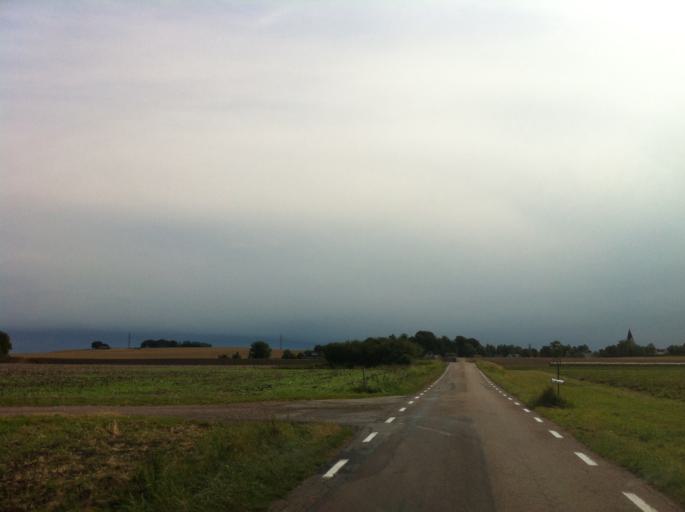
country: SE
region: Skane
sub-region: Landskrona
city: Asmundtorp
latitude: 55.9134
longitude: 12.8807
